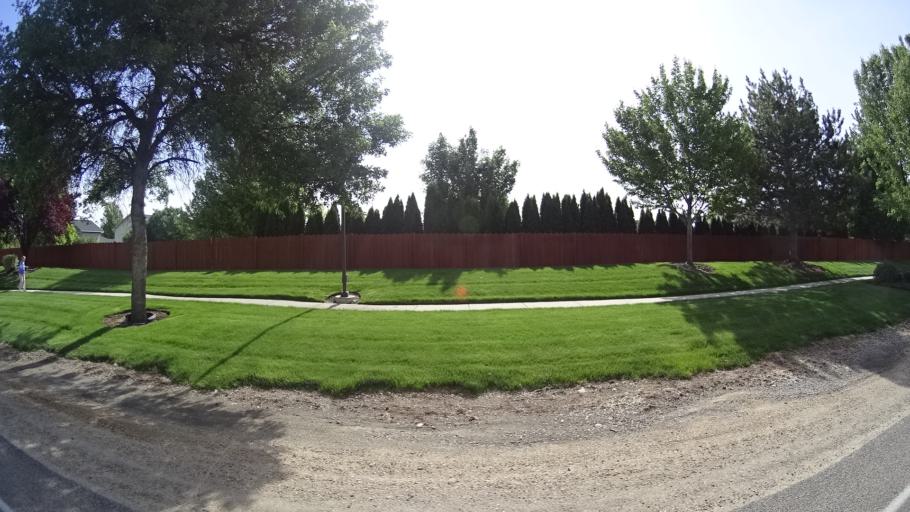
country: US
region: Idaho
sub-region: Ada County
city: Meridian
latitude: 43.5582
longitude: -116.3344
